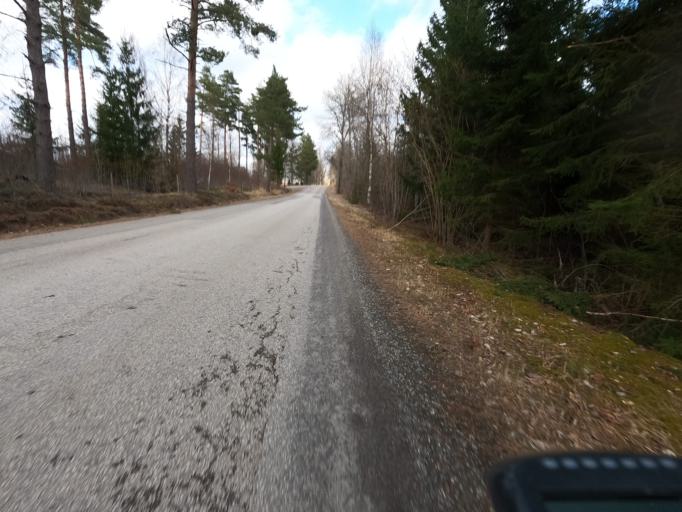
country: SE
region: Kronoberg
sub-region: Alvesta Kommun
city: Vislanda
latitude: 56.8103
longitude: 14.4938
